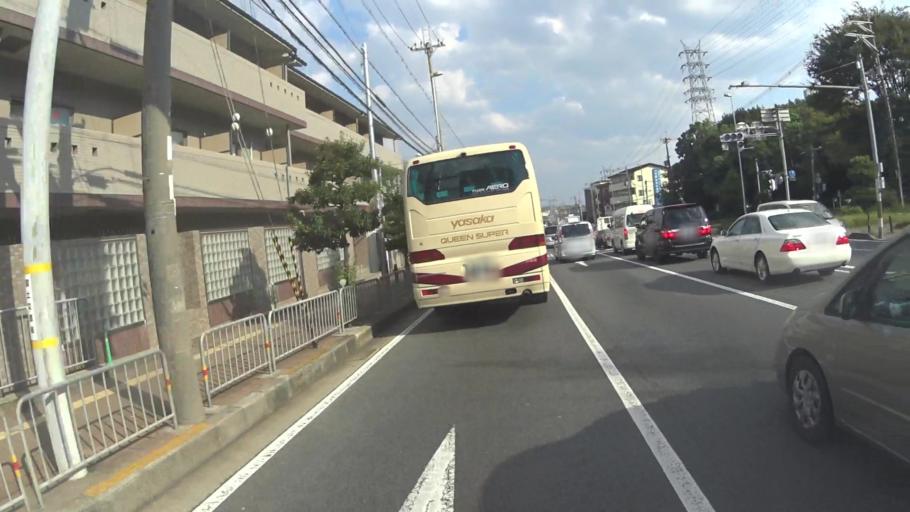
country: JP
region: Kyoto
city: Muko
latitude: 34.9740
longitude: 135.6687
